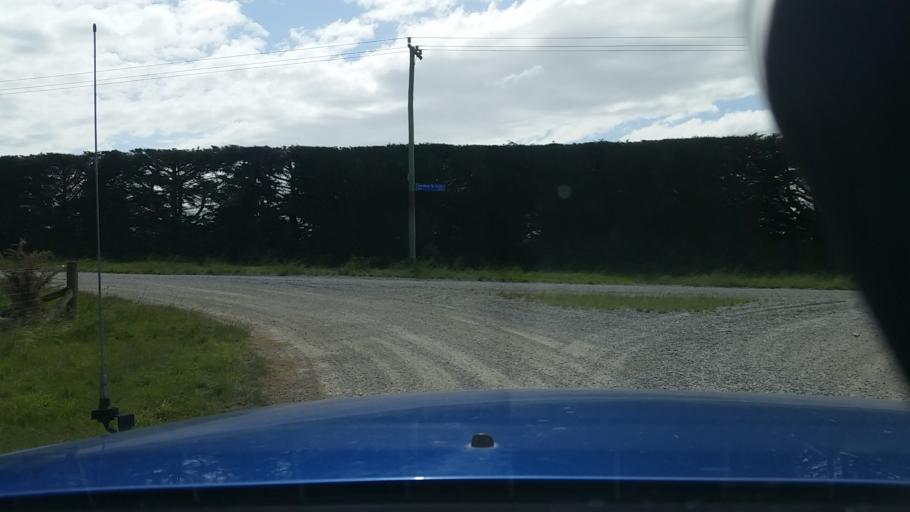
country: NZ
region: Canterbury
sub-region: Ashburton District
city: Ashburton
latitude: -43.9540
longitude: 171.9057
